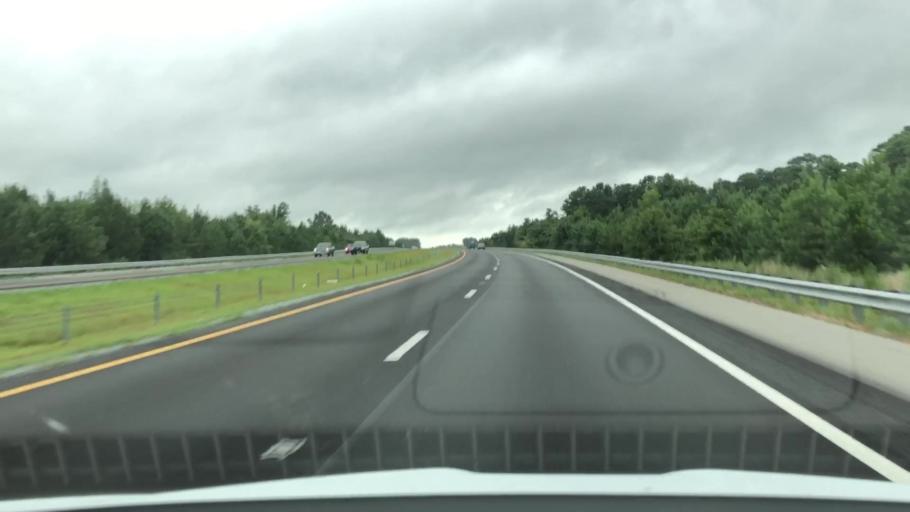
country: US
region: North Carolina
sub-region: Wayne County
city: Goldsboro
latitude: 35.4383
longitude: -77.9844
